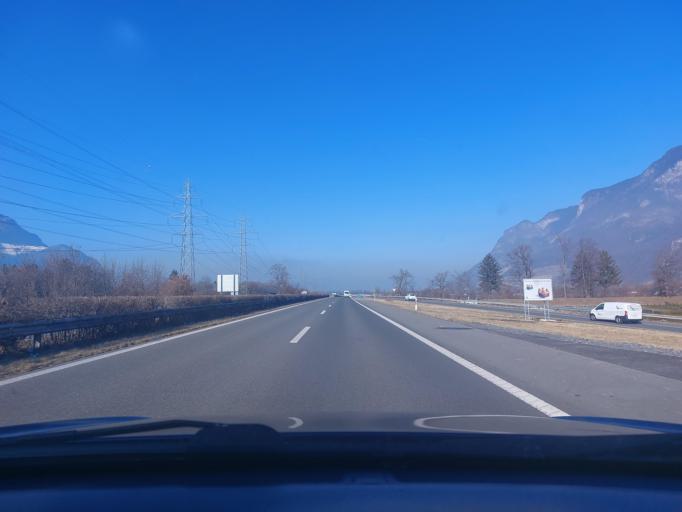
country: CH
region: Vaud
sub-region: Aigle District
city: Aigle
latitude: 46.3222
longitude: 6.9396
